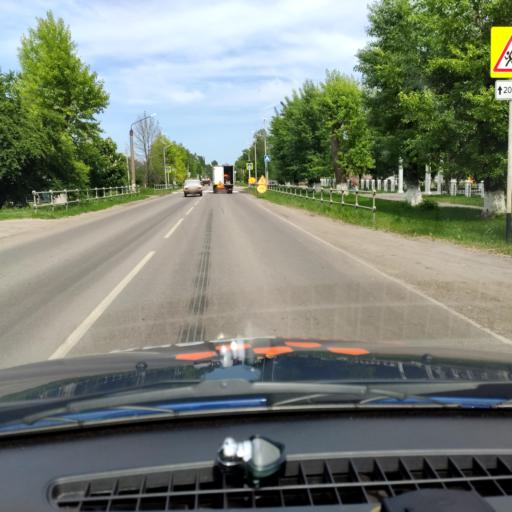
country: RU
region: Voronezj
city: Maslovka
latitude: 51.5383
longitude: 39.3366
